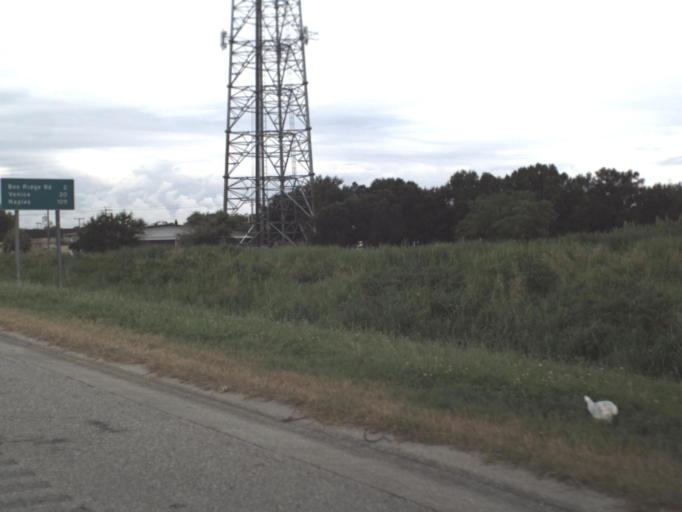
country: US
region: Florida
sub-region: Sarasota County
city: Fruitville
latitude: 27.3283
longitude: -82.4477
